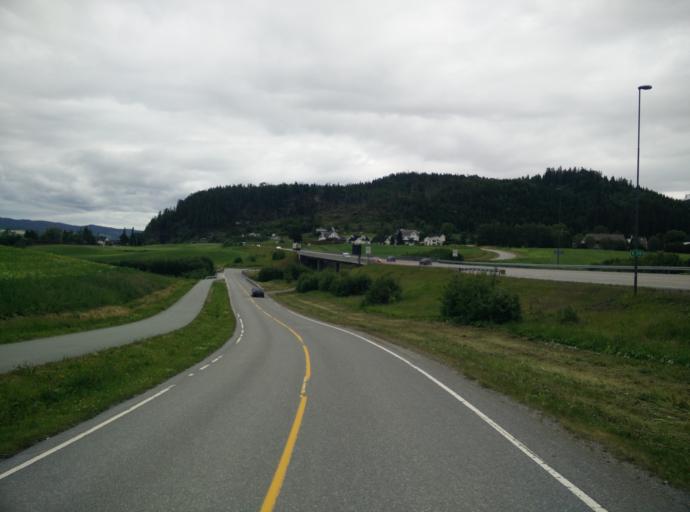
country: NO
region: Sor-Trondelag
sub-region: Skaun
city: Borsa
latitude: 63.3223
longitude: 10.0669
